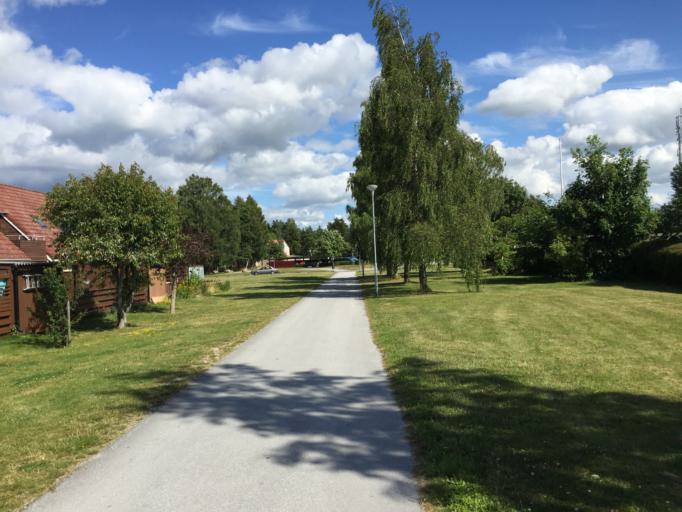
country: SE
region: Gotland
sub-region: Gotland
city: Visby
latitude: 57.6128
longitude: 18.3022
